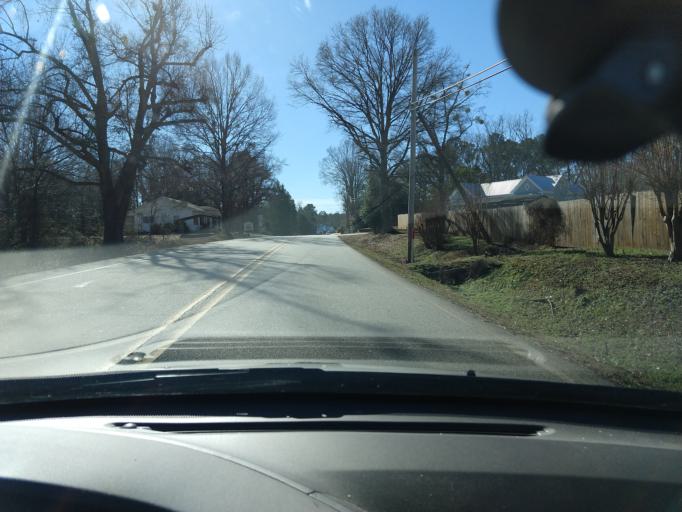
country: US
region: Georgia
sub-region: Walton County
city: Social Circle
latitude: 33.5153
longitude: -83.7329
